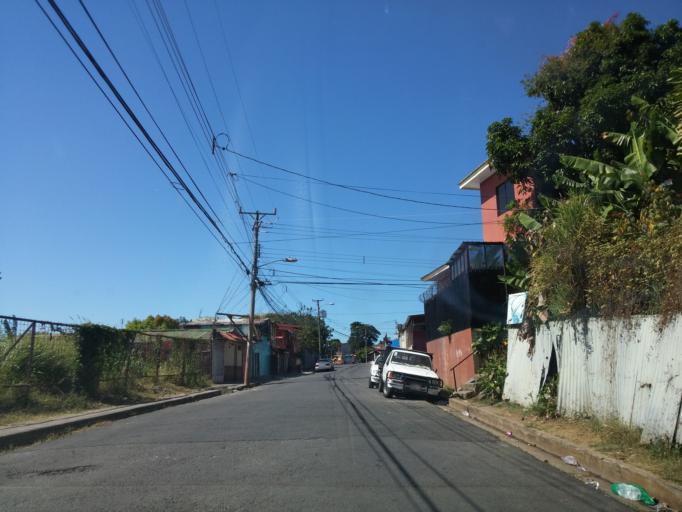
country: CR
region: San Jose
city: San Jose
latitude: 9.9402
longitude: -84.0905
